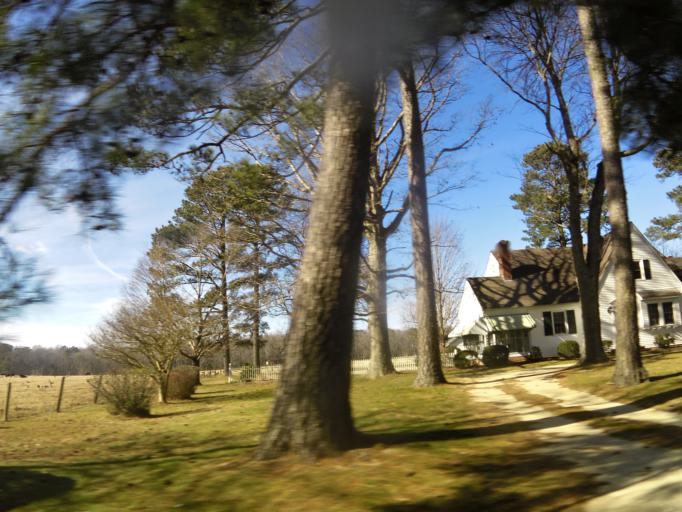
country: US
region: Virginia
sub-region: Isle of Wight County
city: Isle of Wight
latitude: 36.9161
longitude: -76.6978
